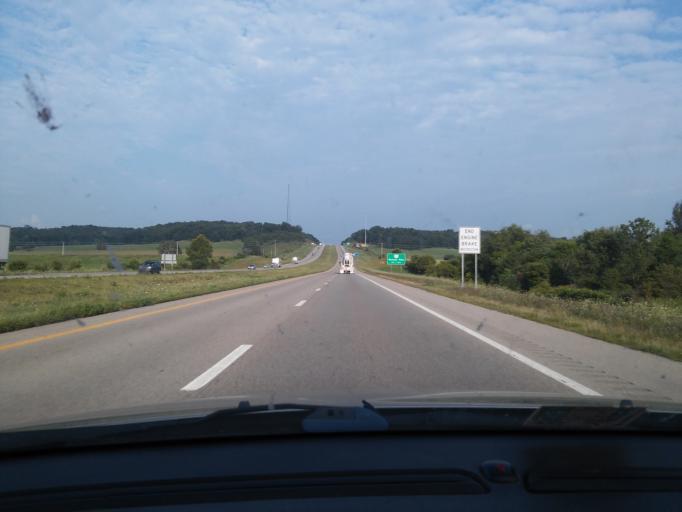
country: US
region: Ohio
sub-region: Gallia County
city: Gallipolis
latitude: 38.8810
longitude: -82.3238
